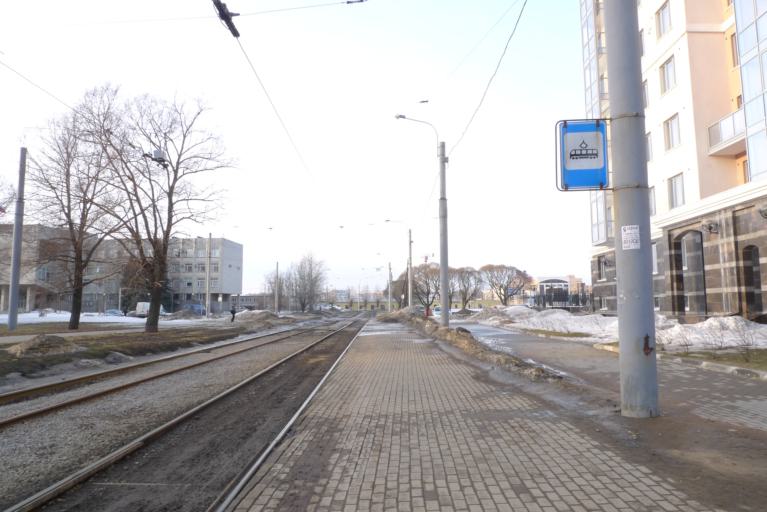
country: RU
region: St.-Petersburg
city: Staraya Derevnya
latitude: 59.9846
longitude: 30.2542
